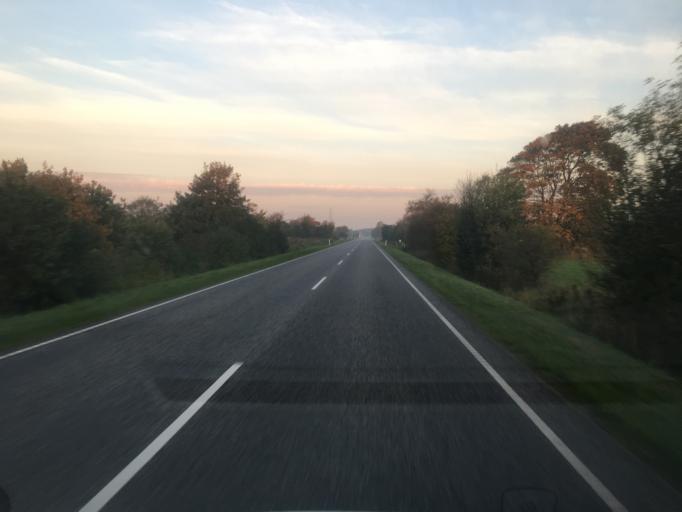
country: DK
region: South Denmark
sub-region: Tonder Kommune
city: Logumkloster
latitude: 55.0348
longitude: 9.0403
